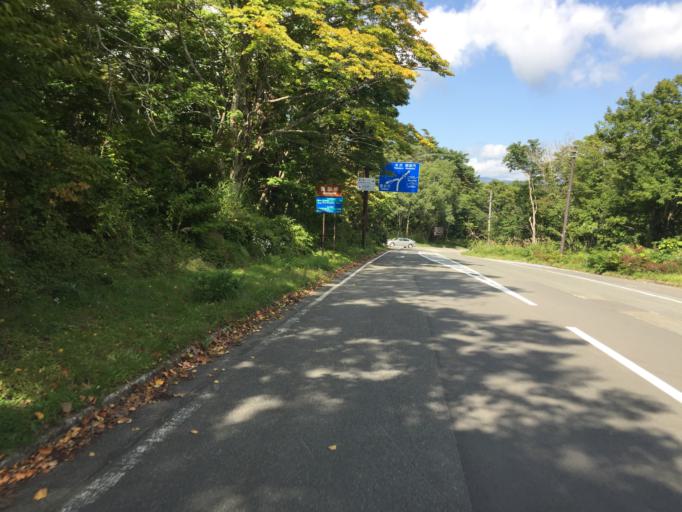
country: JP
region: Fukushima
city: Inawashiro
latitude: 37.6432
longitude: 140.0504
